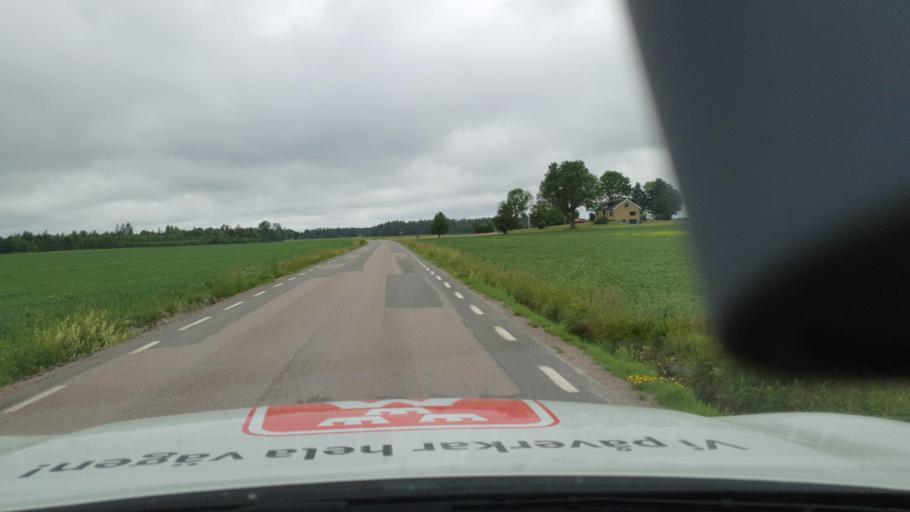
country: SE
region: Vaestra Goetaland
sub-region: Tibro Kommun
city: Tibro
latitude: 58.3941
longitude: 14.0664
